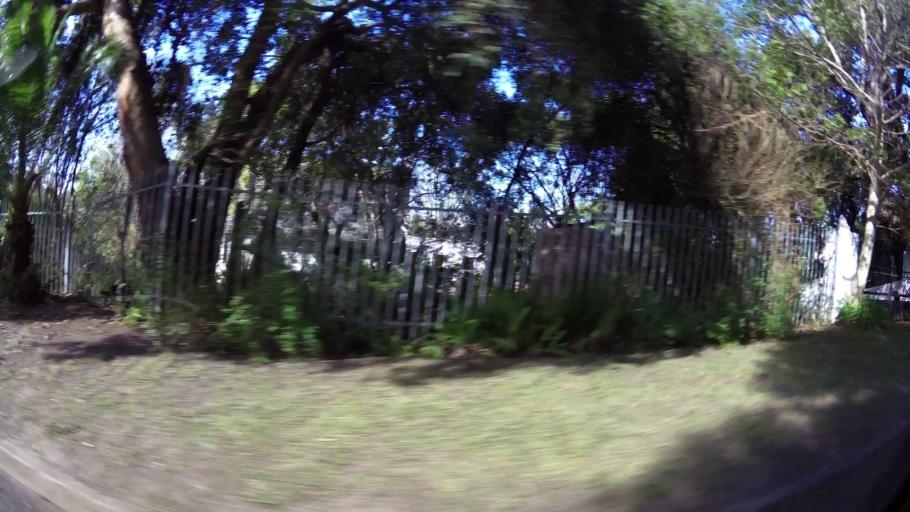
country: ZA
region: Western Cape
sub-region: Eden District Municipality
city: George
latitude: -33.9445
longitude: 22.4664
